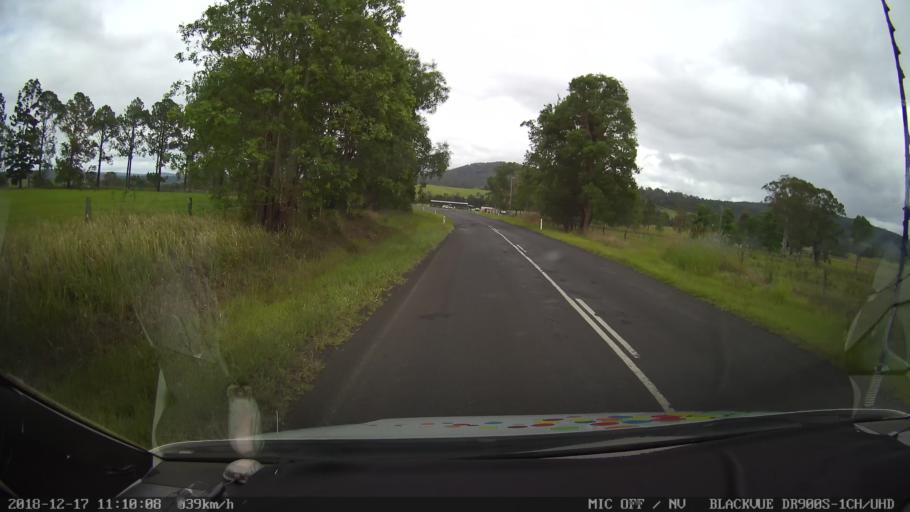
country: AU
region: New South Wales
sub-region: Kyogle
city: Kyogle
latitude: -28.7505
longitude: 152.6522
